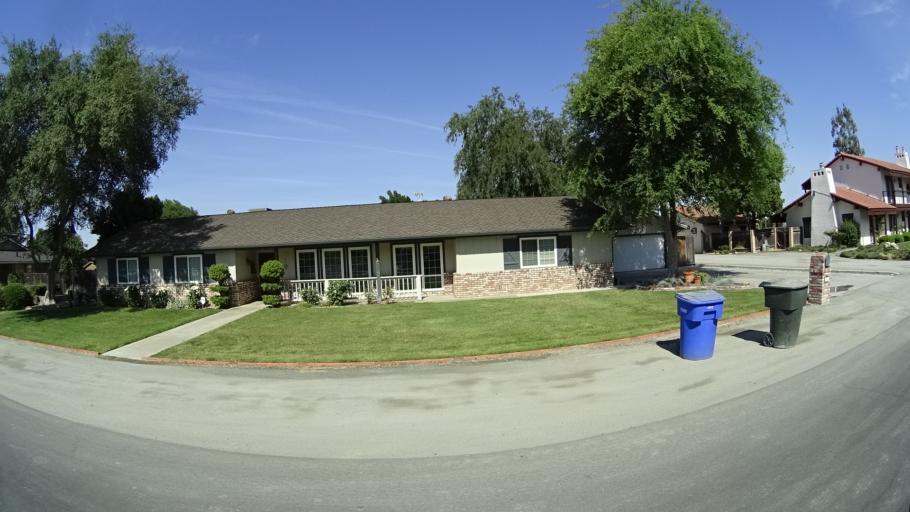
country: US
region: California
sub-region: Kings County
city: Hanford
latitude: 36.3457
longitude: -119.6656
